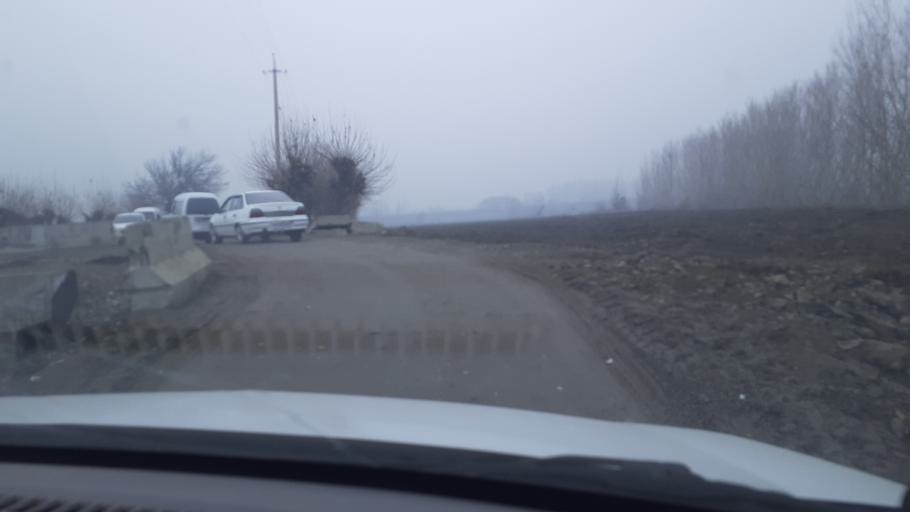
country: UZ
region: Namangan
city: Haqqulobod
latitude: 40.9008
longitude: 71.9977
